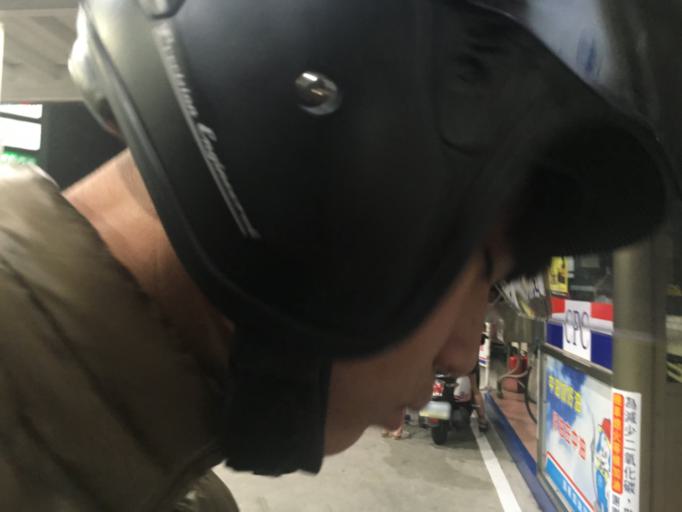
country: TW
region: Taiwan
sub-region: Hsinchu
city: Hsinchu
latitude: 24.7545
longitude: 120.9540
